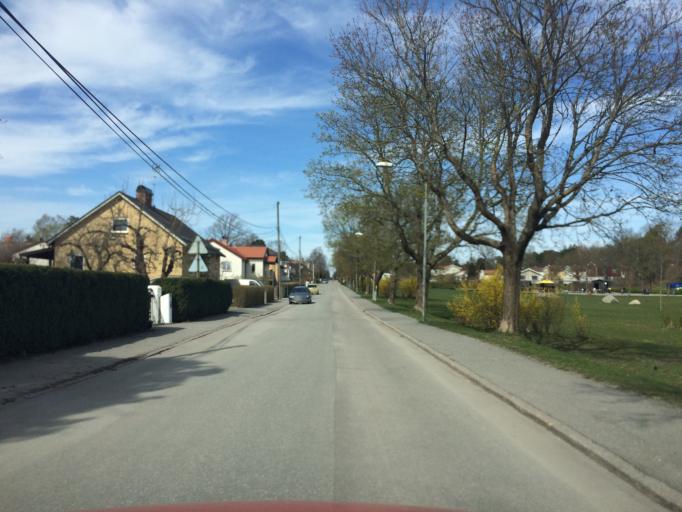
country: SE
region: Stockholm
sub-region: Huddinge Kommun
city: Huddinge
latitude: 59.2777
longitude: 17.9900
